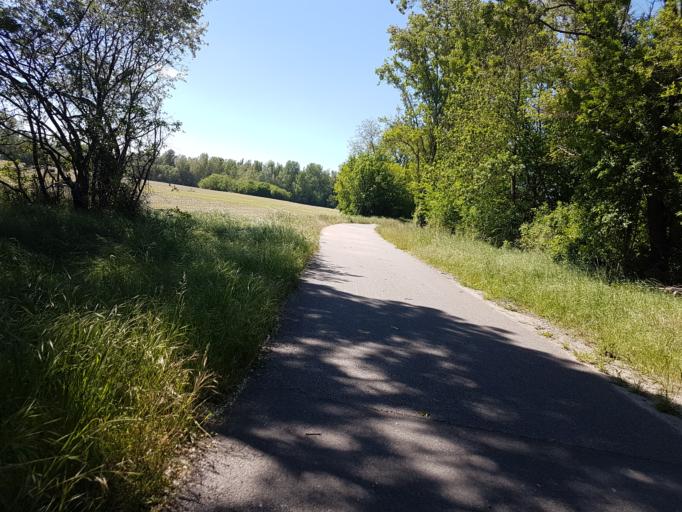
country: FR
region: Rhone-Alpes
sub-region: Departement de la Drome
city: Andancette
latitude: 45.2584
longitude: 4.8104
